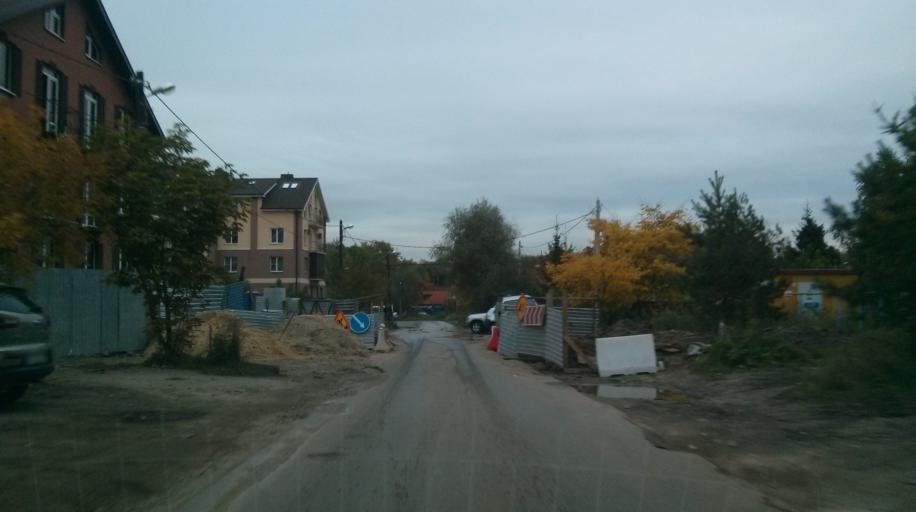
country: RU
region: Nizjnij Novgorod
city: Nizhniy Novgorod
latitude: 56.3050
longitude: 44.0412
